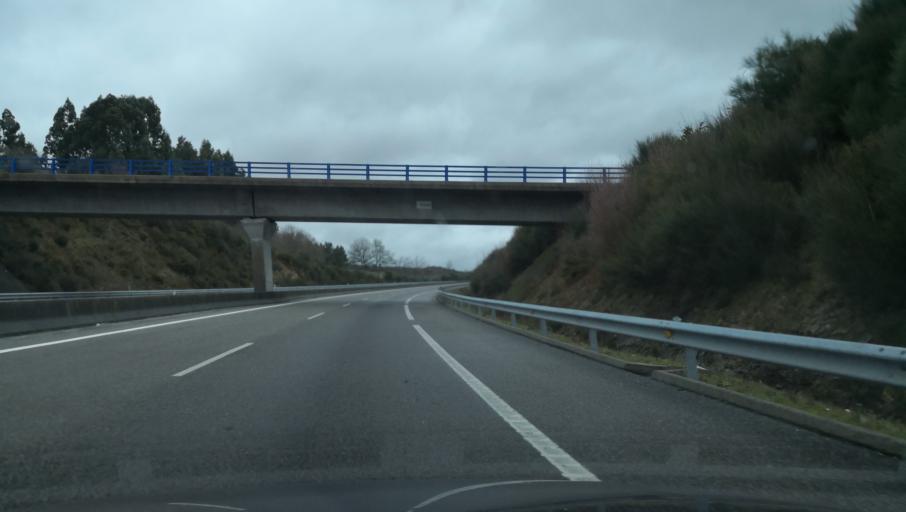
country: ES
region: Galicia
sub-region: Provincia de Pontevedra
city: Dozon
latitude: 42.5446
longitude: -8.0203
